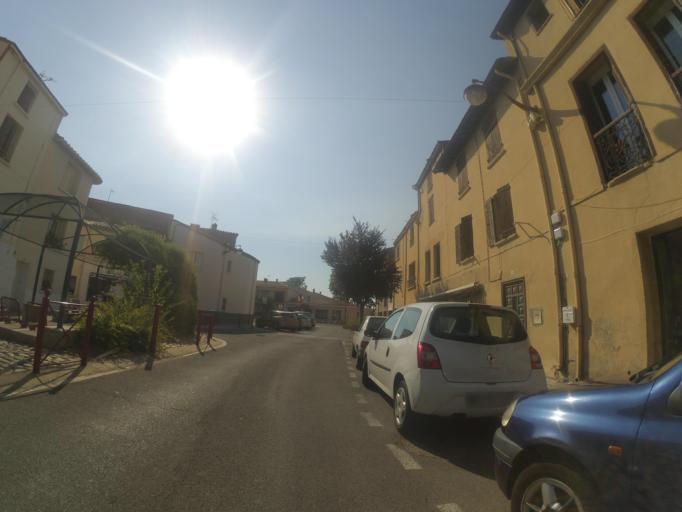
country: FR
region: Languedoc-Roussillon
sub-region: Departement des Pyrenees-Orientales
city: Toulouges
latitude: 42.6705
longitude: 2.8302
